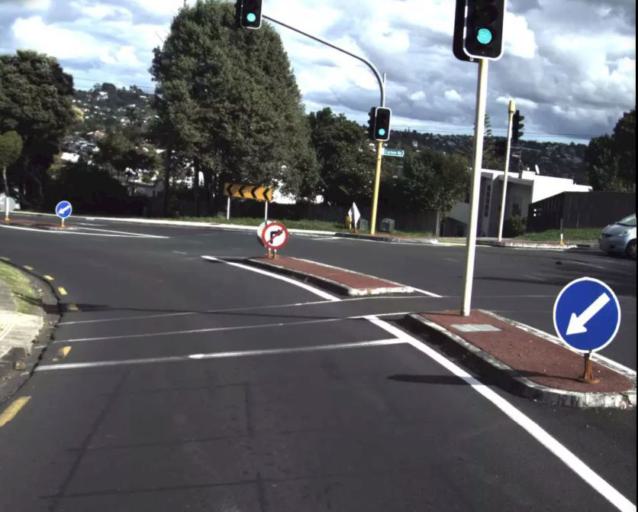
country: NZ
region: Auckland
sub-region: Auckland
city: Rothesay Bay
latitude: -36.7112
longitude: 174.7448
